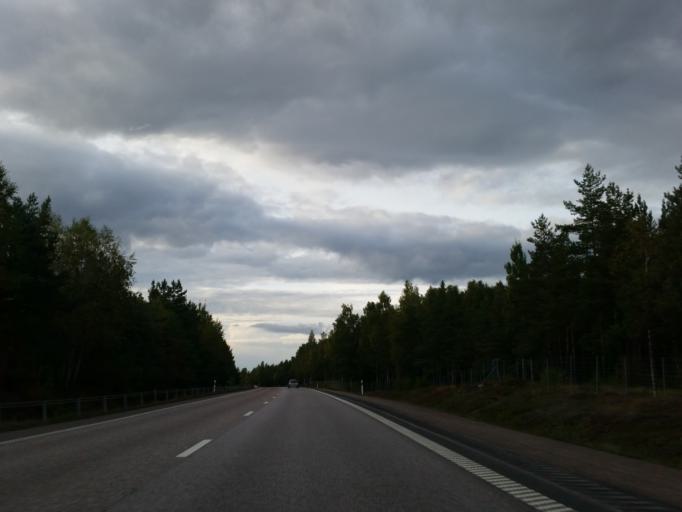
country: SE
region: Stockholm
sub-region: Sigtuna Kommun
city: Marsta
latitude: 59.6940
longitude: 17.8670
